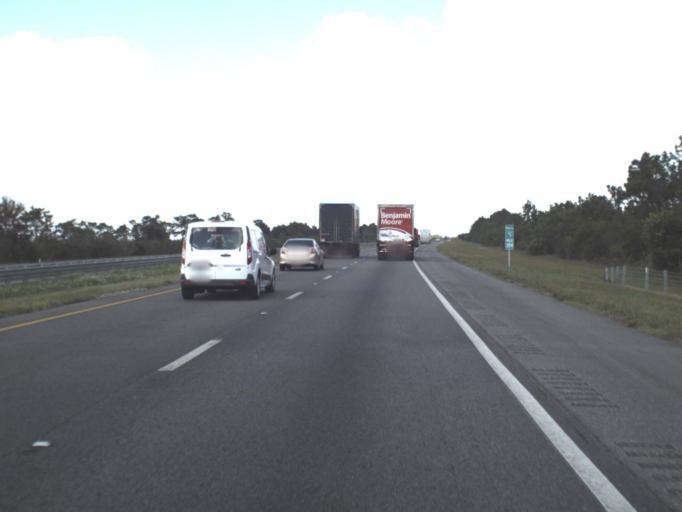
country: US
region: Florida
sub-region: Indian River County
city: Fellsmere
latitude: 27.8161
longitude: -81.0024
